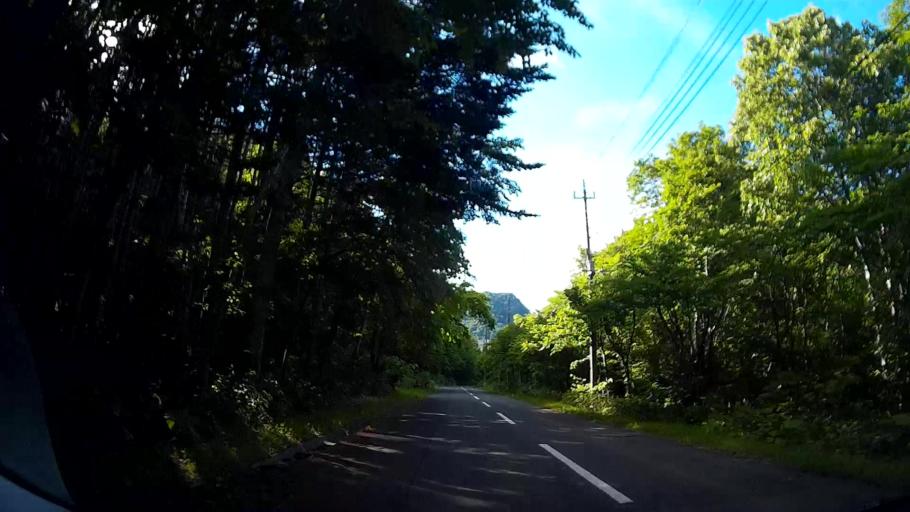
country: JP
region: Hokkaido
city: Sapporo
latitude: 42.9772
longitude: 141.1636
